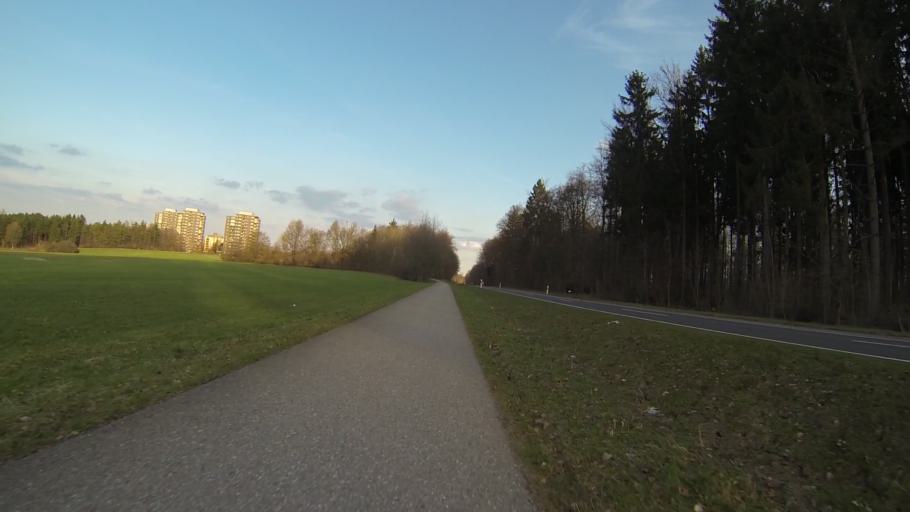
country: DE
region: Baden-Wuerttemberg
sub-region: Regierungsbezirk Stuttgart
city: Heidenheim an der Brenz
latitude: 48.6989
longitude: 10.1282
